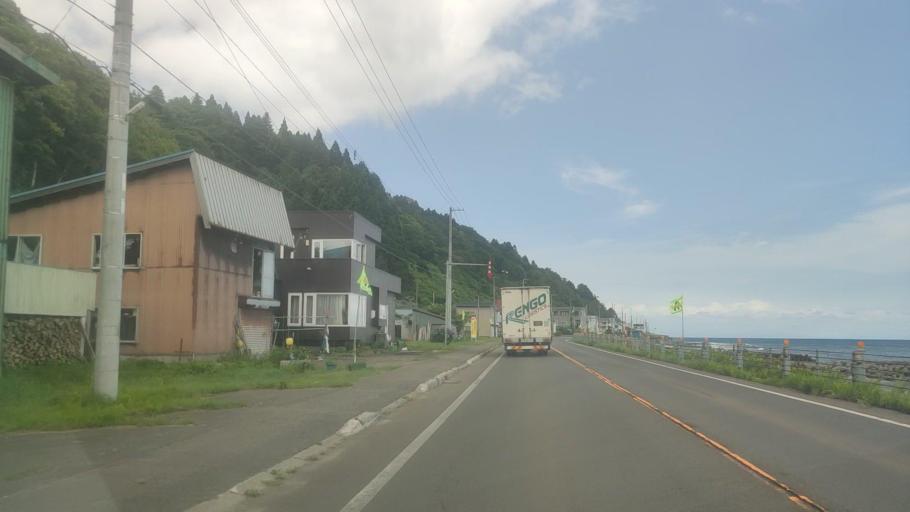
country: JP
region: Hokkaido
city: Nanae
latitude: 42.1403
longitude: 140.5037
